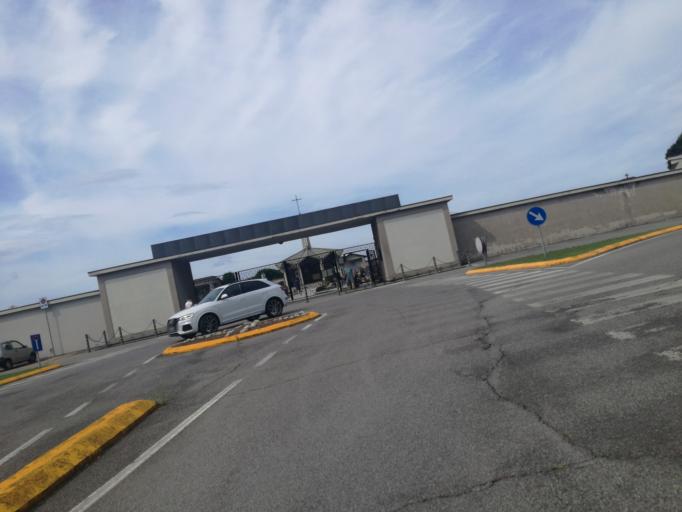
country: IT
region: Lombardy
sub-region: Provincia di Bergamo
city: Calusco d'Adda
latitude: 45.6876
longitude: 9.4626
